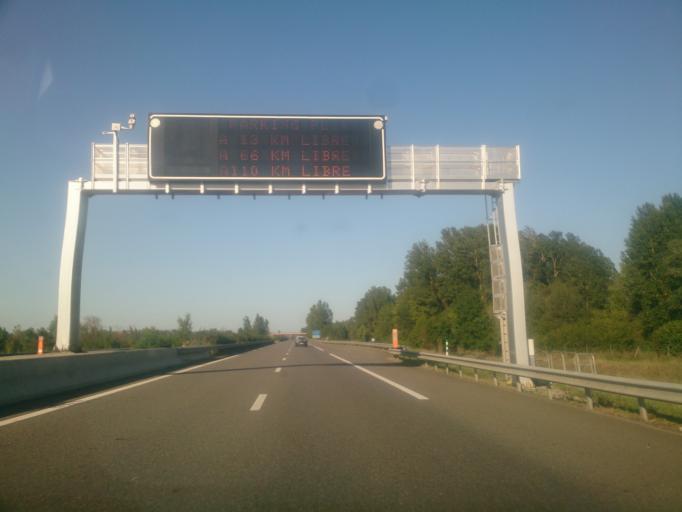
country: FR
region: Midi-Pyrenees
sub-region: Departement du Tarn-et-Garonne
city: Realville
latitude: 44.1321
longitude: 1.4867
